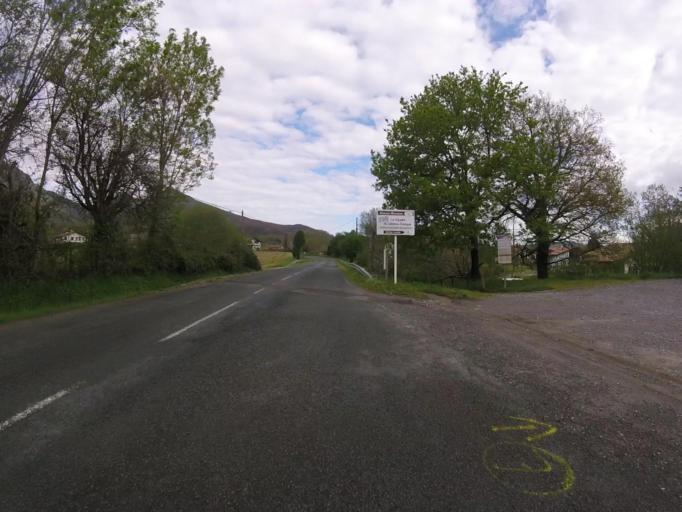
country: FR
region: Aquitaine
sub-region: Departement des Pyrenees-Atlantiques
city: Sare
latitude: 43.2996
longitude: -1.5894
